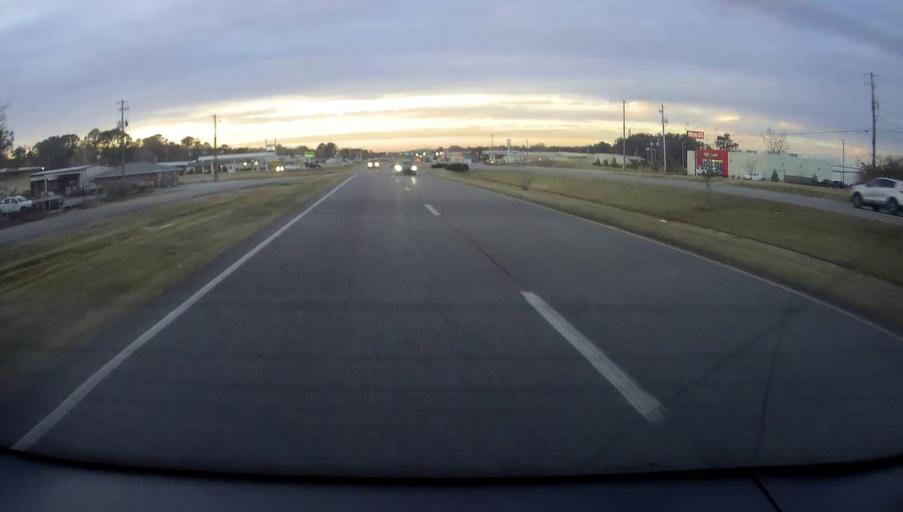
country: US
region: Alabama
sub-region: Etowah County
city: Glencoe
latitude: 33.9626
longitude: -85.9387
